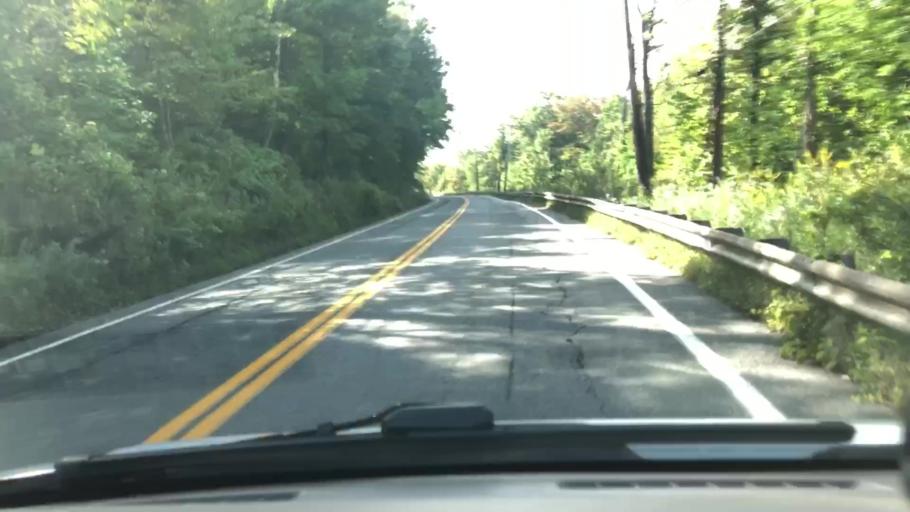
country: US
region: Massachusetts
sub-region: Berkshire County
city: North Adams
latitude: 42.7029
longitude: -73.0652
